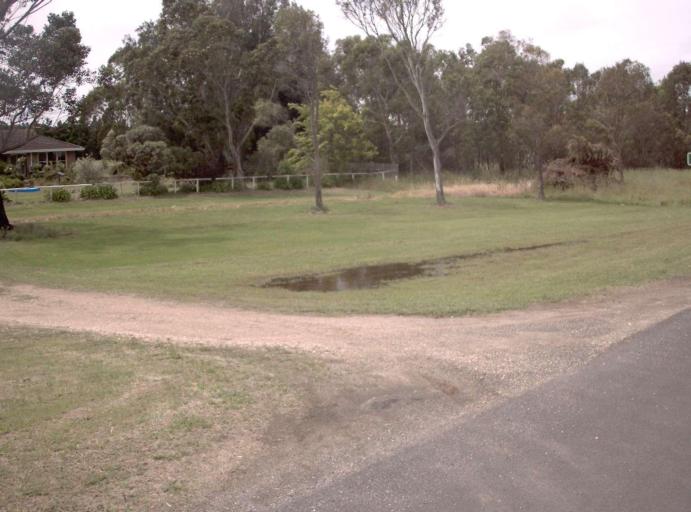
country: AU
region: Victoria
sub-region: Wellington
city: Sale
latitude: -38.0629
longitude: 147.0290
